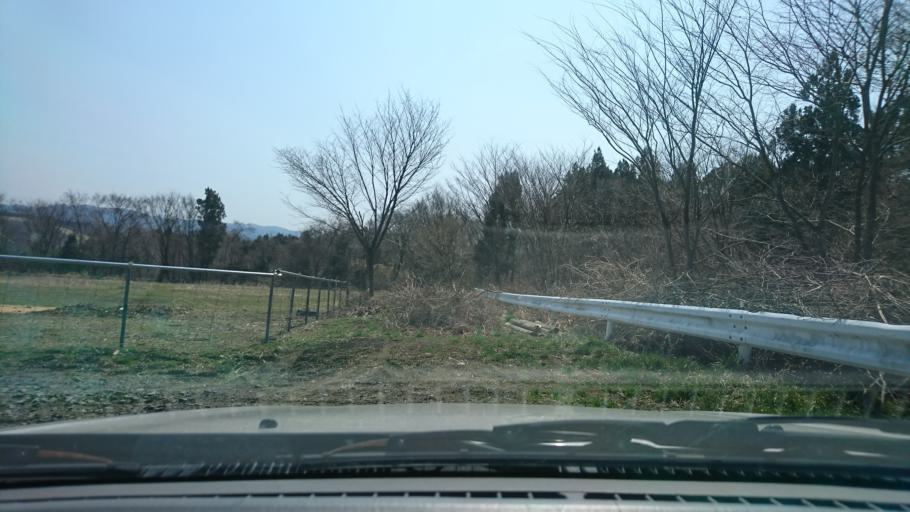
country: JP
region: Iwate
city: Ichinoseki
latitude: 38.8174
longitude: 141.2614
